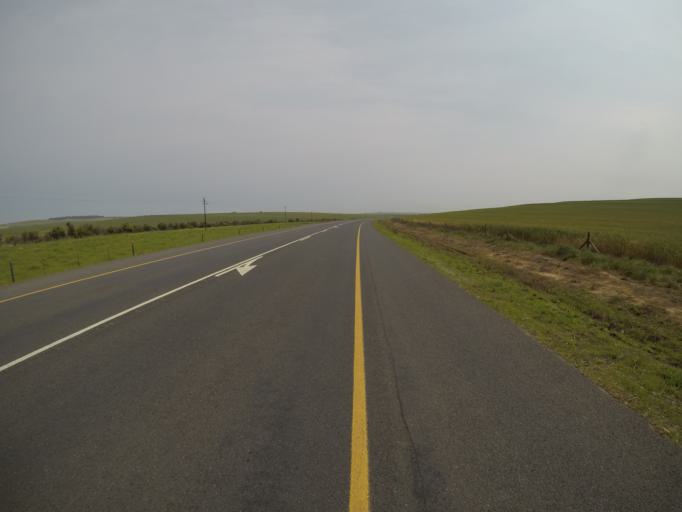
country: ZA
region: Western Cape
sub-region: West Coast District Municipality
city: Malmesbury
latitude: -33.4752
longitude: 18.7989
